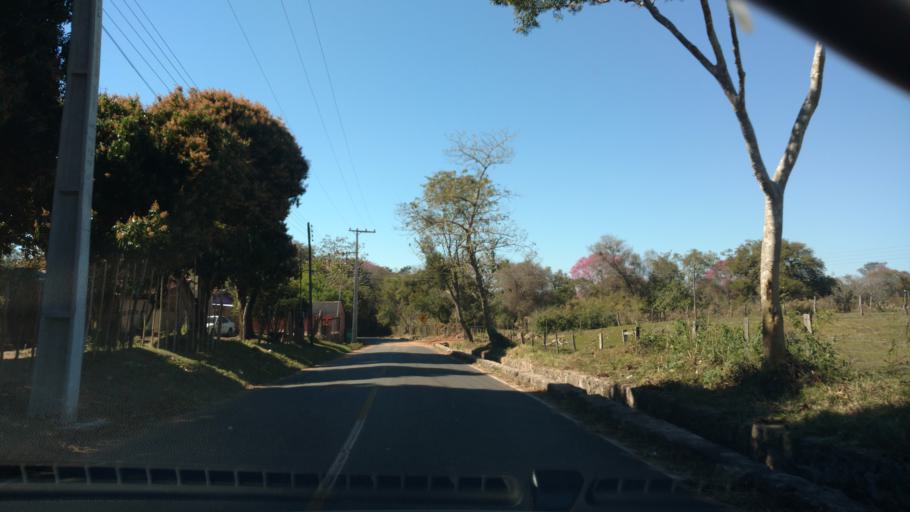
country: PY
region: Central
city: Ypacarai
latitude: -25.4157
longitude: -57.2983
